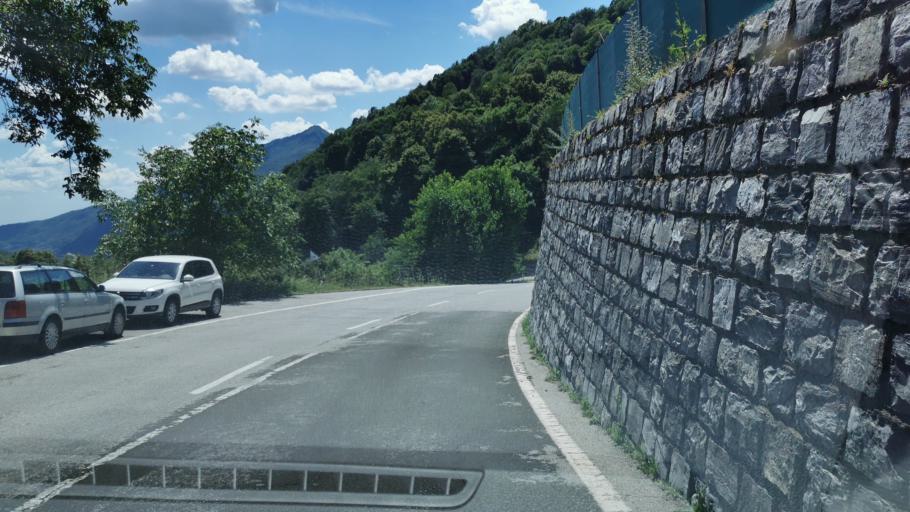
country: IT
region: Lombardy
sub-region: Provincia di Como
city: Campione
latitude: 45.9560
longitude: 8.9844
